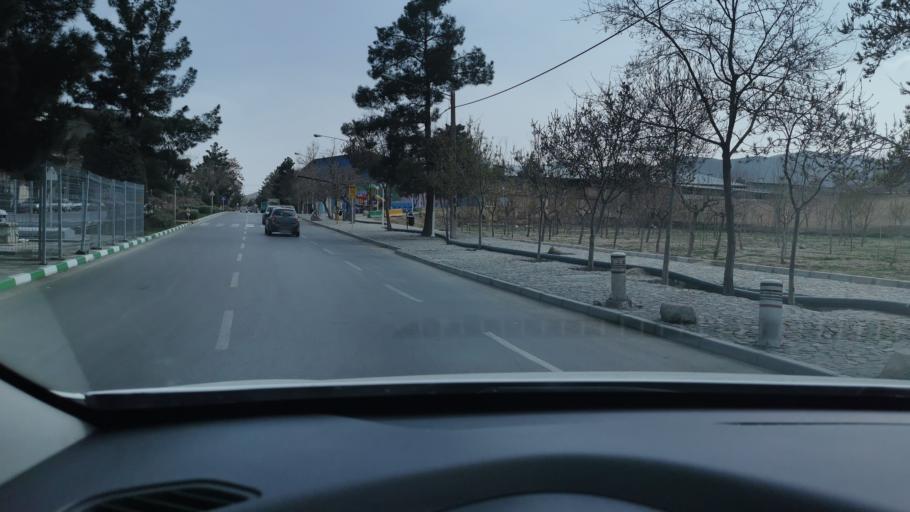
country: IR
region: Razavi Khorasan
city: Mashhad
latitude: 36.2797
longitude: 59.5644
